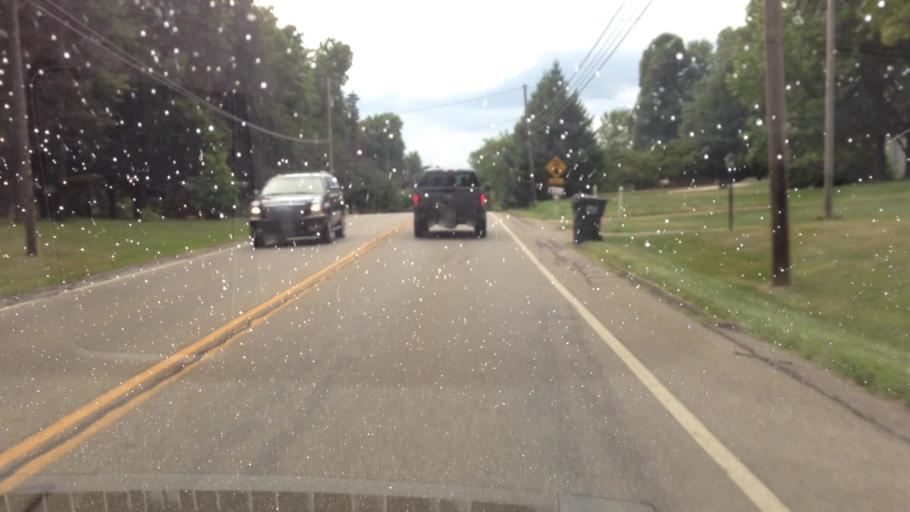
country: US
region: Ohio
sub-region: Stark County
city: Uniontown
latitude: 40.9761
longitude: -81.4345
